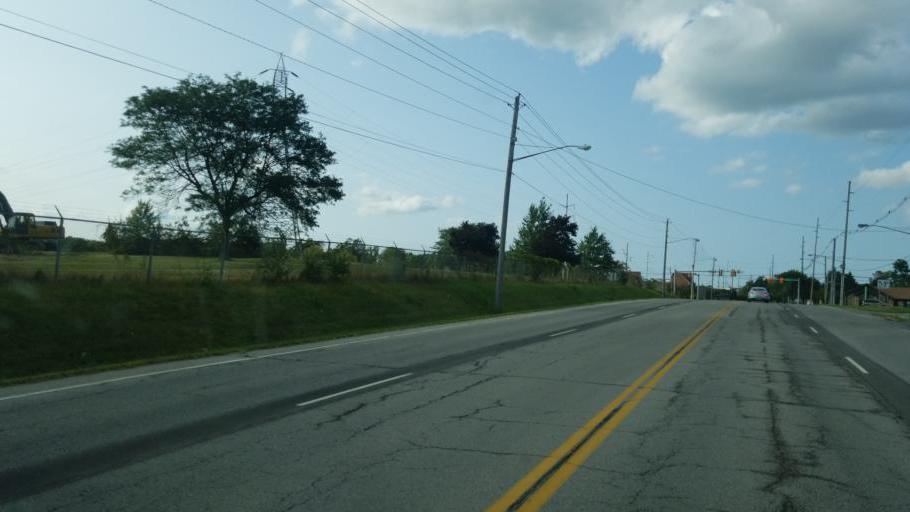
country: US
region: Ohio
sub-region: Richland County
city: Ontario
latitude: 40.7719
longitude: -82.5973
